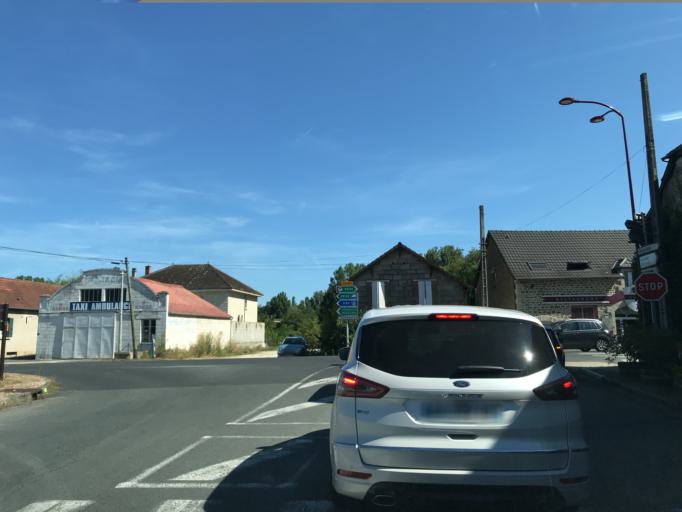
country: FR
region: Limousin
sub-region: Departement de la Correze
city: Larche
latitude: 45.1230
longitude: 1.4118
